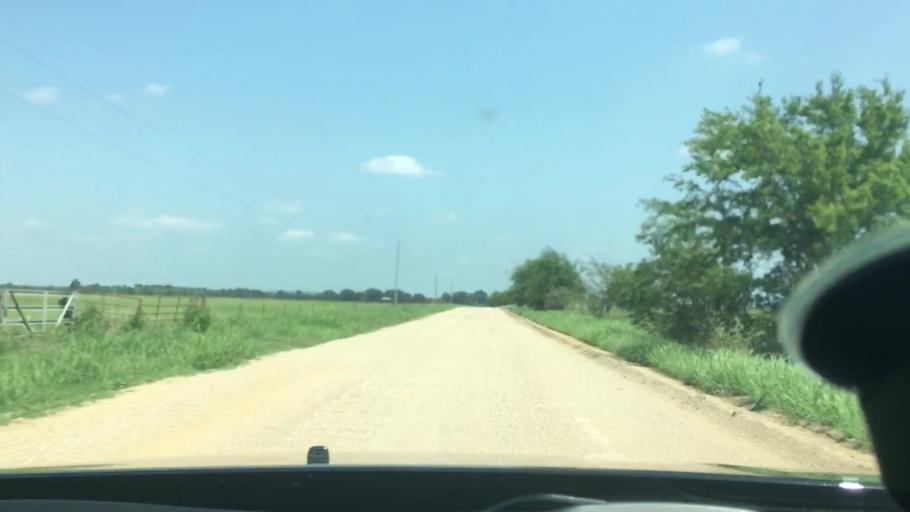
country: US
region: Oklahoma
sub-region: Coal County
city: Coalgate
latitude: 34.4330
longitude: -96.4314
